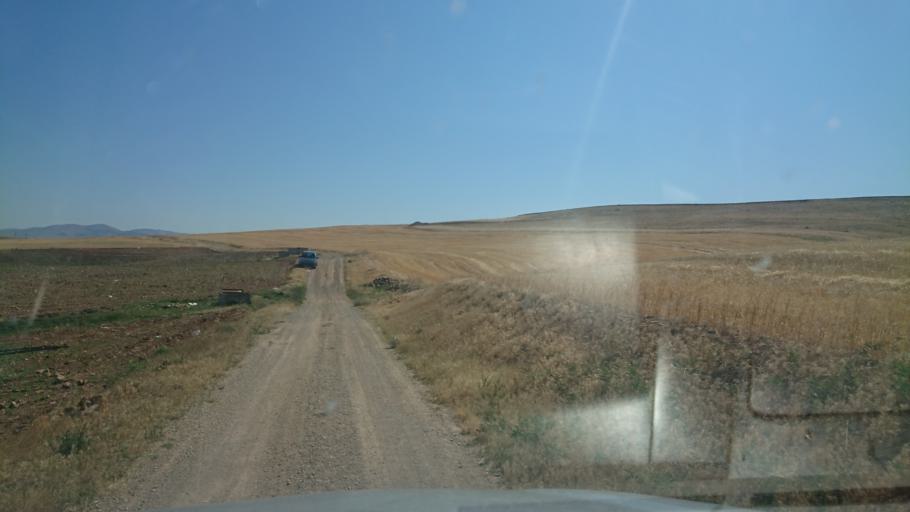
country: TR
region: Ankara
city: Evren
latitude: 39.0525
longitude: 33.8789
